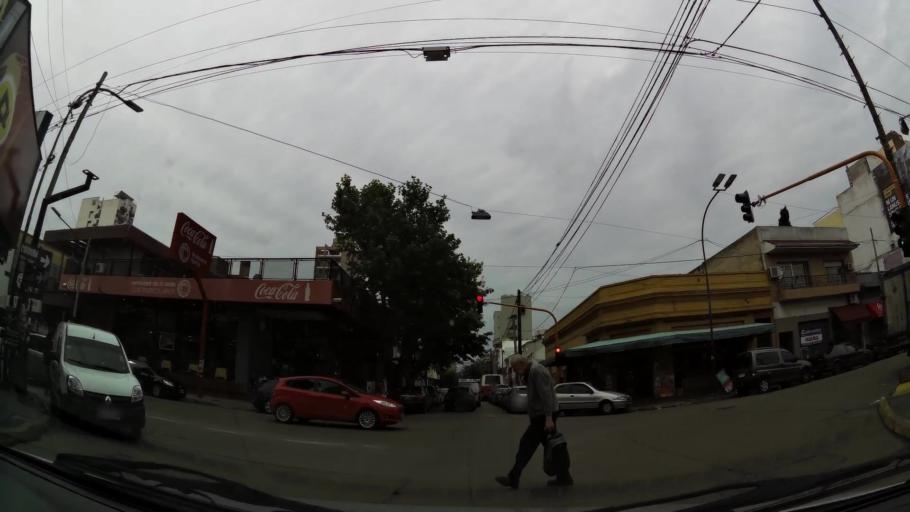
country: AR
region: Buenos Aires
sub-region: Partido de Lanus
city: Lanus
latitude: -34.7119
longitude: -58.3849
